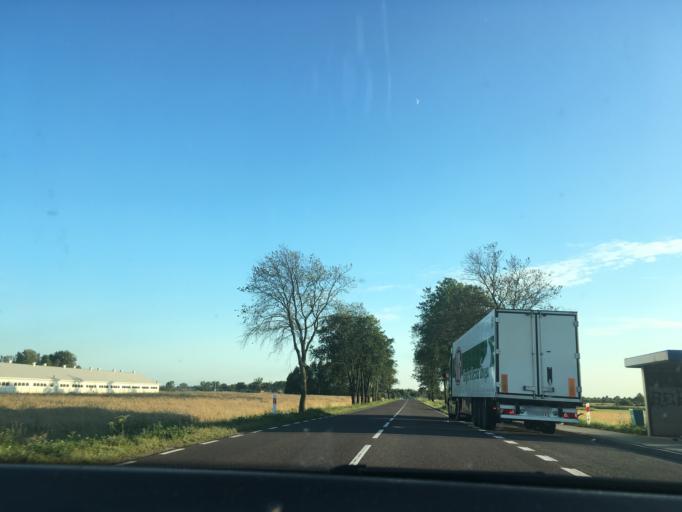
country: PL
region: Lublin Voivodeship
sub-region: Powiat bialski
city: Rzeczyca
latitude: 51.9223
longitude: 22.7097
